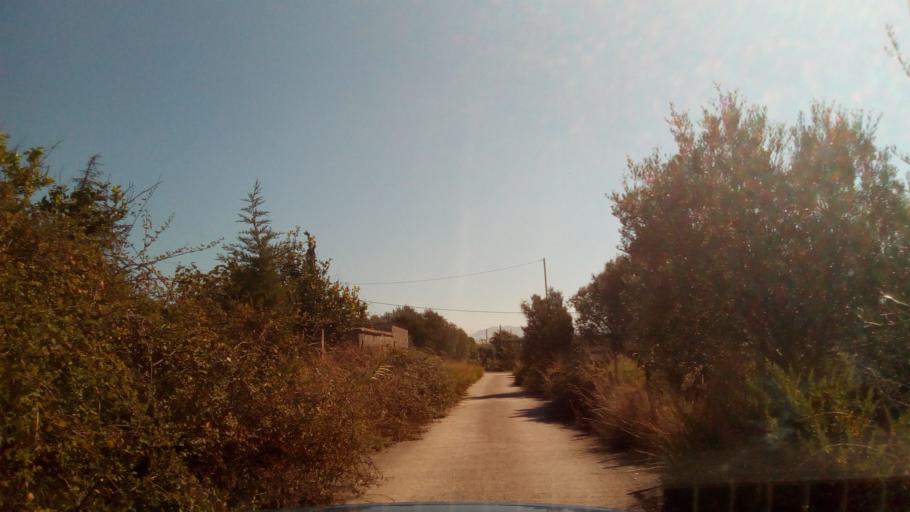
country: GR
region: West Greece
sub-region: Nomos Aitolias kai Akarnanias
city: Antirrio
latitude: 38.3351
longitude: 21.7515
